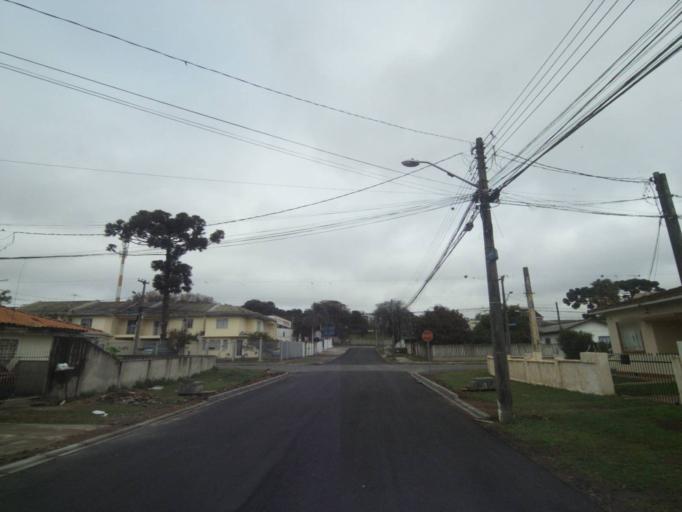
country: BR
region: Parana
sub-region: Curitiba
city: Curitiba
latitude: -25.5047
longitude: -49.2867
